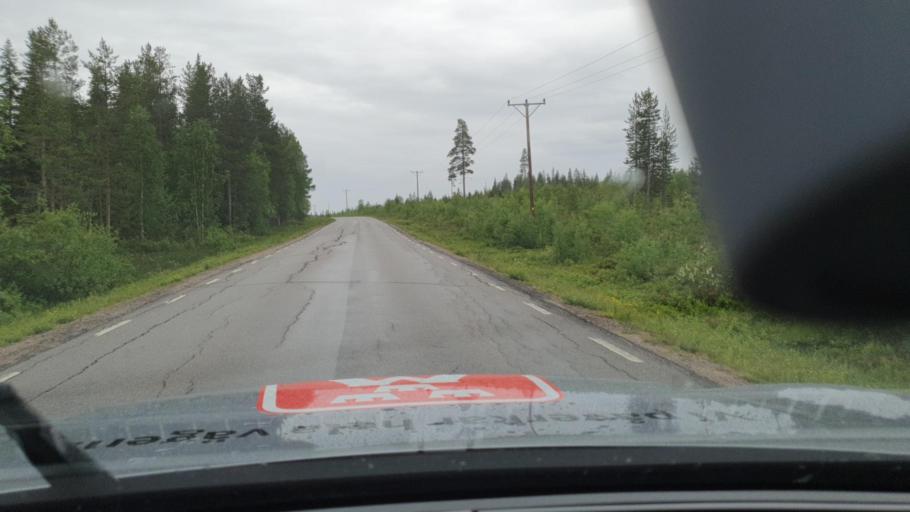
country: SE
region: Norrbotten
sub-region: Pajala Kommun
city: Pajala
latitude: 66.7896
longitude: 23.1269
